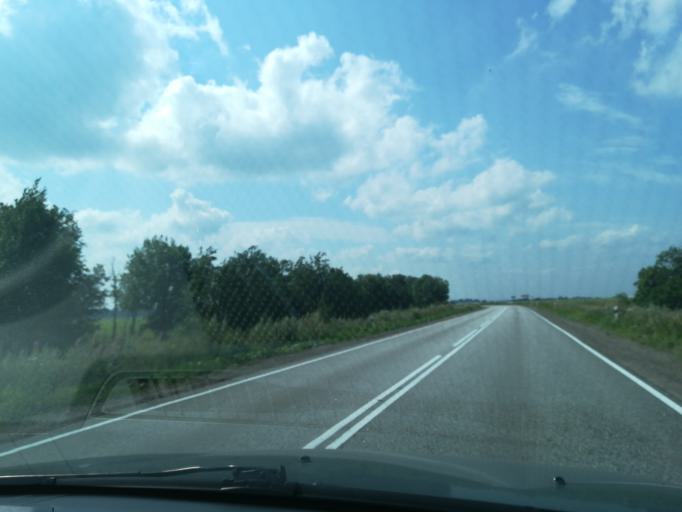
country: RU
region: Leningrad
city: Kopor'ye
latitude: 59.6849
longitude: 29.0361
